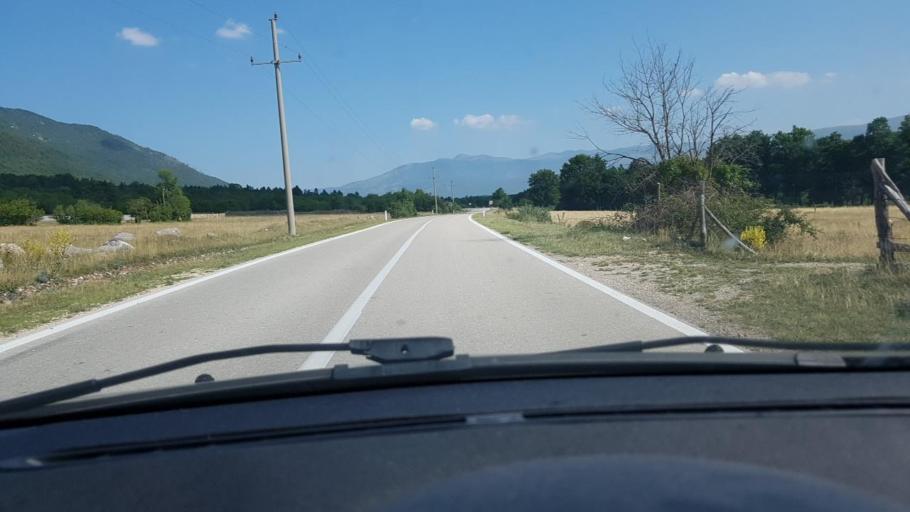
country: HR
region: Splitsko-Dalmatinska
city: Hrvace
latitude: 44.0102
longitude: 16.6035
